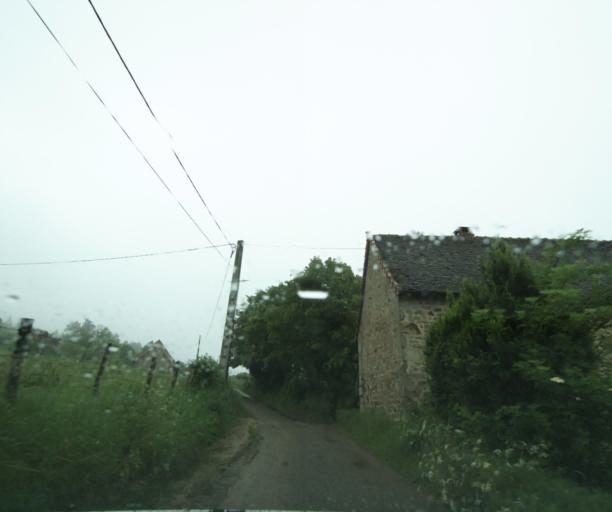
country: FR
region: Bourgogne
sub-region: Departement de Saone-et-Loire
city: La Clayette
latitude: 46.3679
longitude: 4.3503
